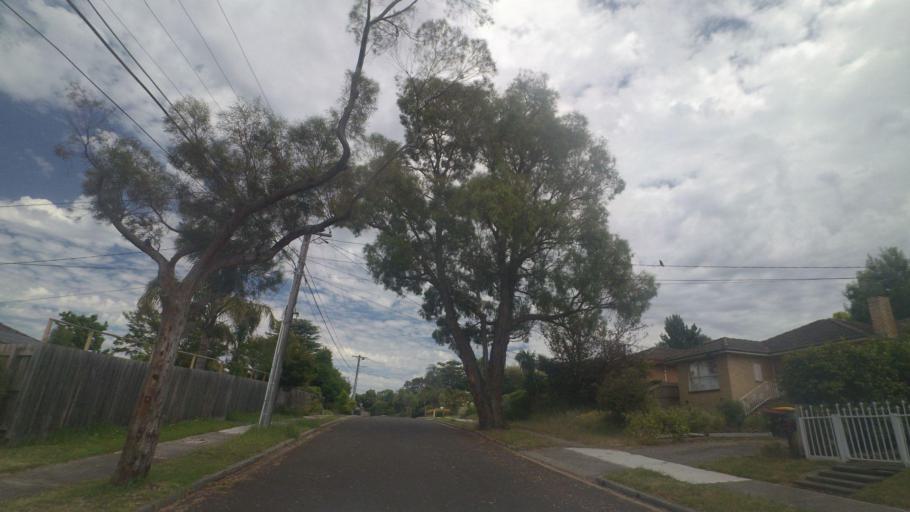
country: AU
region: Victoria
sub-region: Banyule
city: Viewbank
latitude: -37.7395
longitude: 145.0855
